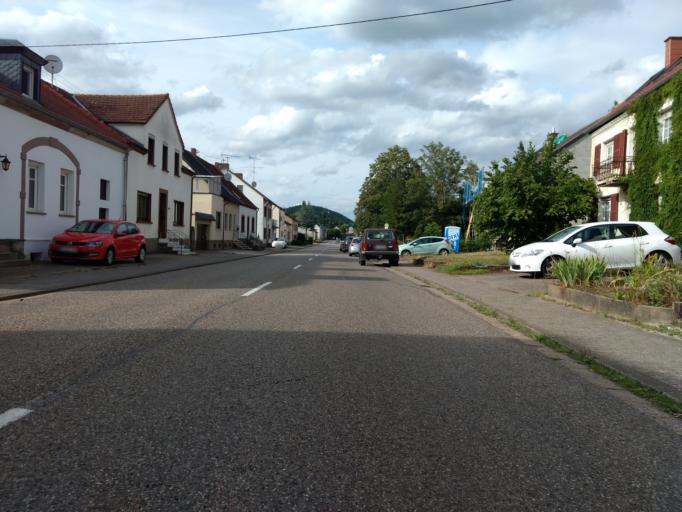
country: DE
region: Saarland
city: Beckingen
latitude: 49.4145
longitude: 6.7257
